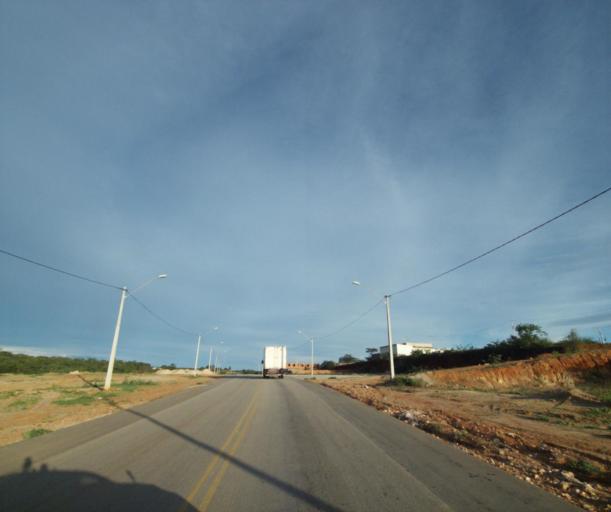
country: BR
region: Bahia
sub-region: Cacule
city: Cacule
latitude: -14.2088
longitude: -42.1058
